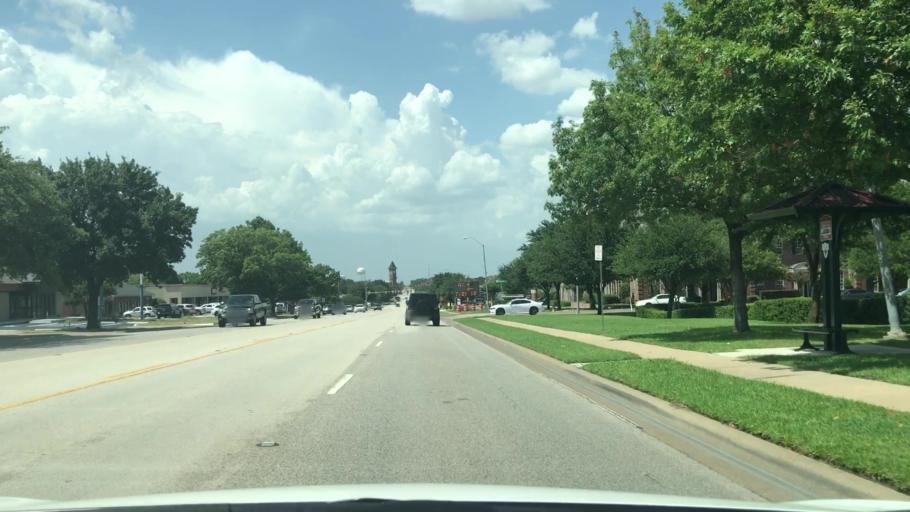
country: US
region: Texas
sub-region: Tarrant County
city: Grapevine
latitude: 32.9261
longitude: -97.0783
